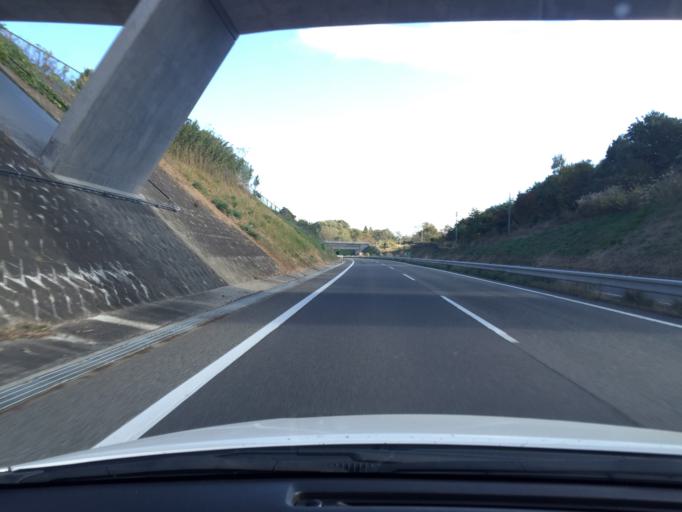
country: JP
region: Fukushima
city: Koriyama
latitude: 37.4470
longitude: 140.4149
